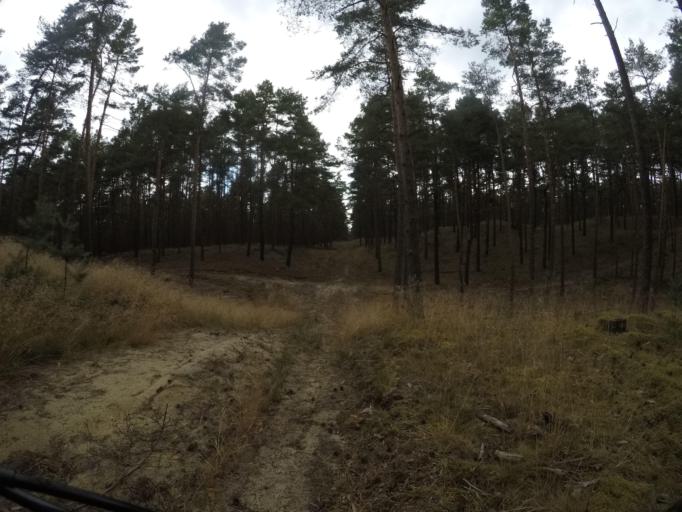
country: DE
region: Lower Saxony
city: Hitzacker
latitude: 53.1939
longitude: 11.0636
